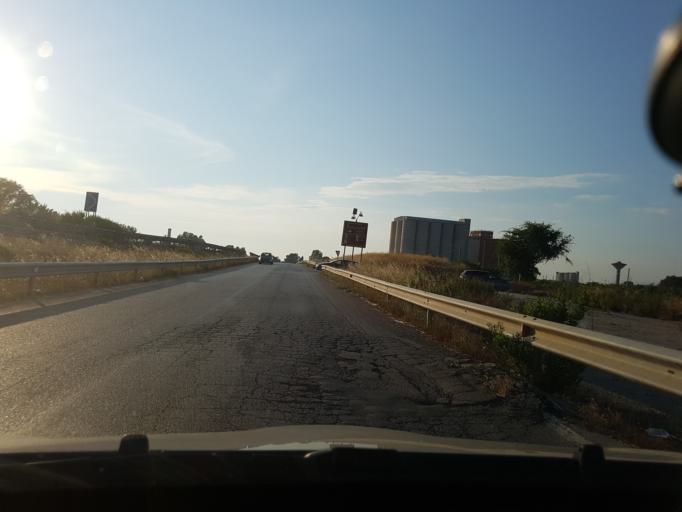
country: IT
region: Apulia
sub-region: Provincia di Foggia
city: Carapelle
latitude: 41.3996
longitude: 15.6539
